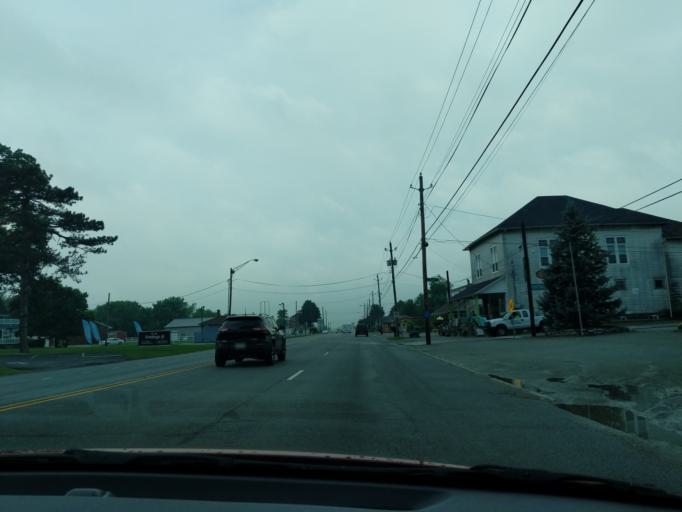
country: US
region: Indiana
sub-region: Hancock County
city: McCordsville
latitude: 39.8942
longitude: -85.9231
